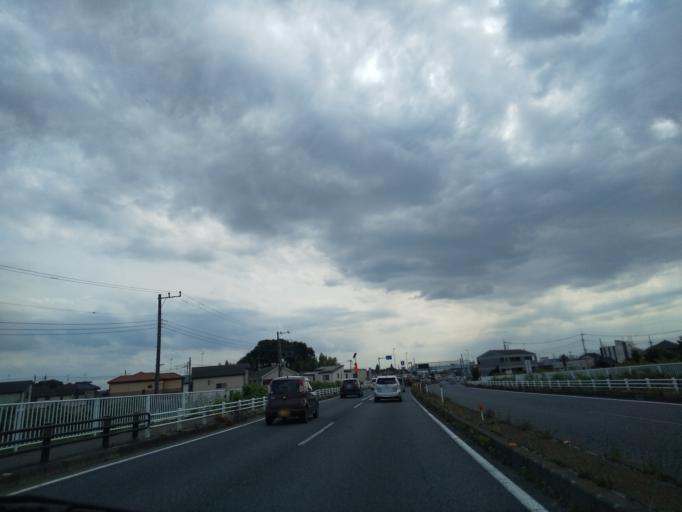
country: JP
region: Chiba
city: Noda
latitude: 35.9893
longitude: 139.8148
